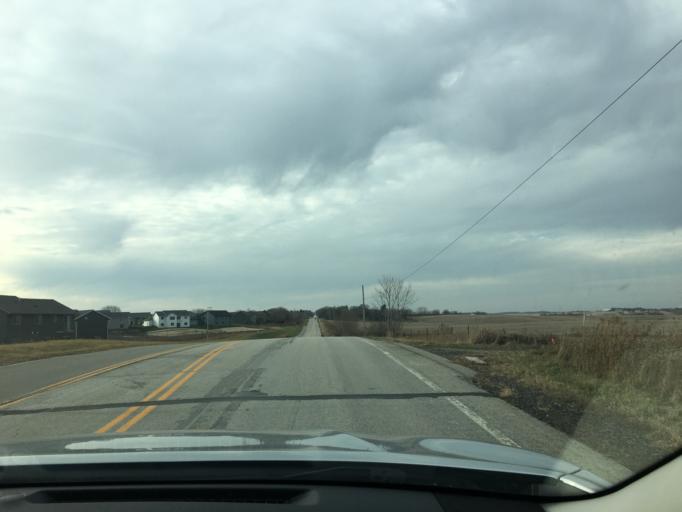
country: US
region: Minnesota
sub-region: Olmsted County
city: Oronoco
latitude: 44.0939
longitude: -92.5243
